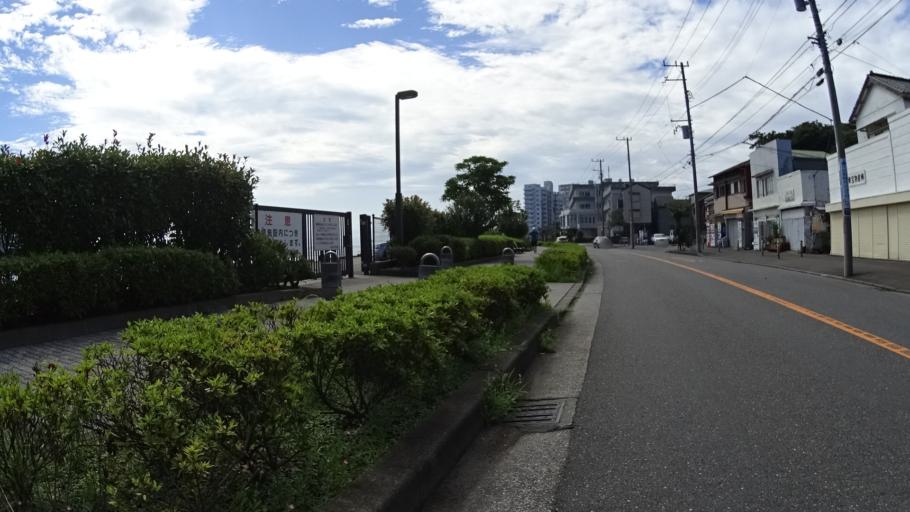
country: JP
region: Kanagawa
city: Yokosuka
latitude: 35.2403
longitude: 139.7200
